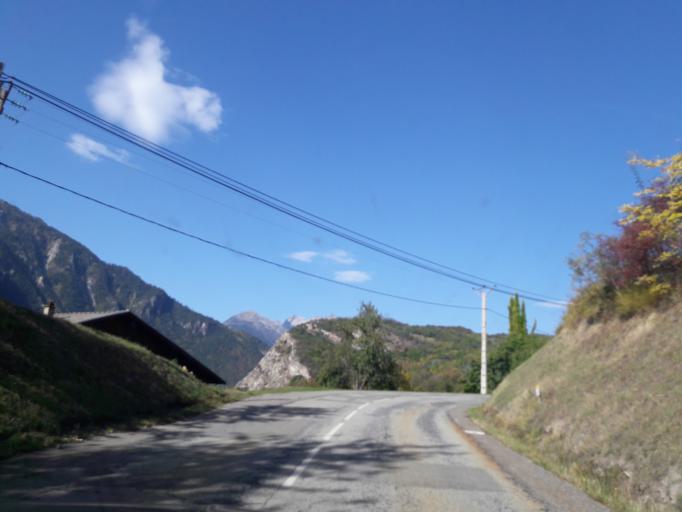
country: FR
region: Rhone-Alpes
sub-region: Departement de la Savoie
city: Saint-Jean-de-Maurienne
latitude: 45.3168
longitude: 6.3494
